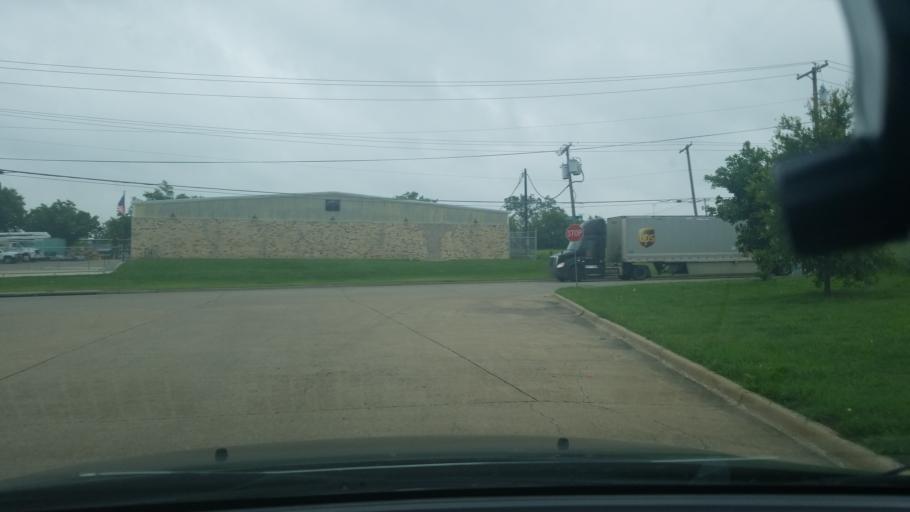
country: US
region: Texas
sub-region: Dallas County
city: Mesquite
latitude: 32.7858
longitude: -96.6564
